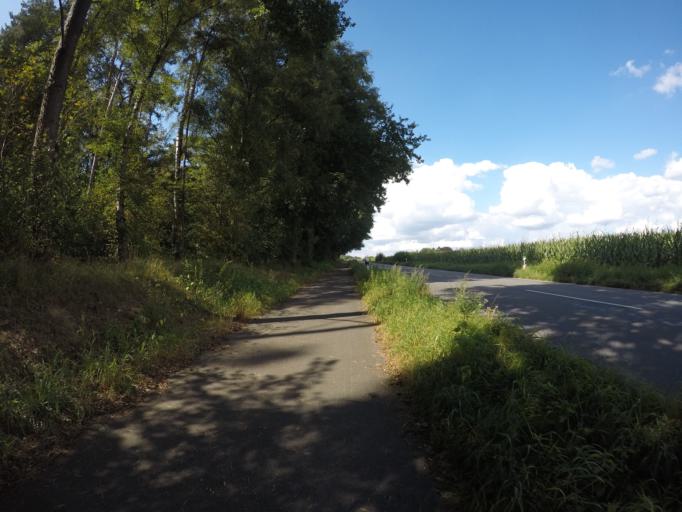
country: DE
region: North Rhine-Westphalia
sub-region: Regierungsbezirk Dusseldorf
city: Mehrhoog
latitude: 51.7469
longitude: 6.5409
